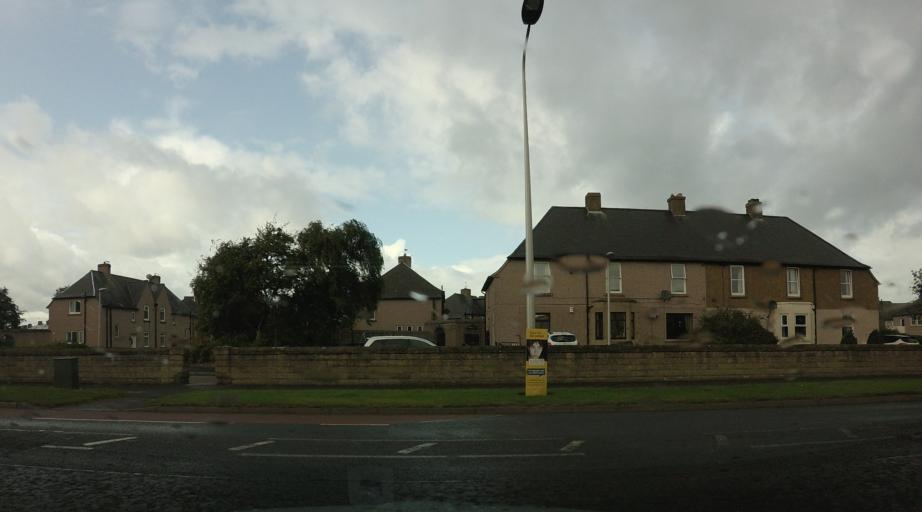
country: GB
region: Scotland
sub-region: East Lothian
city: Musselburgh
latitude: 55.9430
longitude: -3.0284
